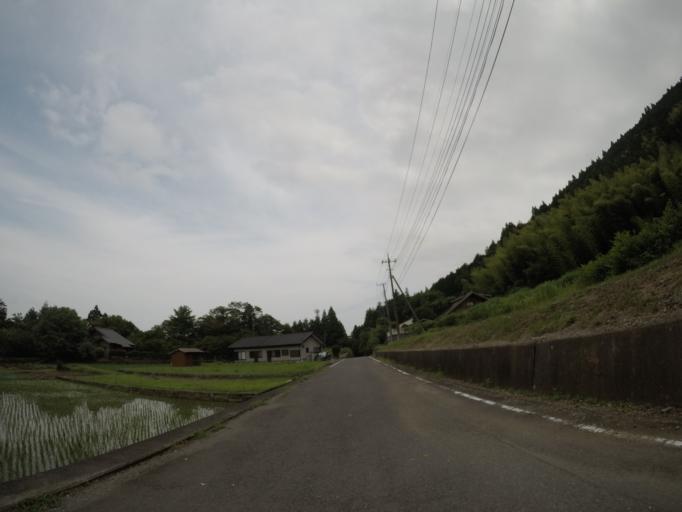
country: JP
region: Shizuoka
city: Fujinomiya
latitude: 35.2375
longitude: 138.5582
